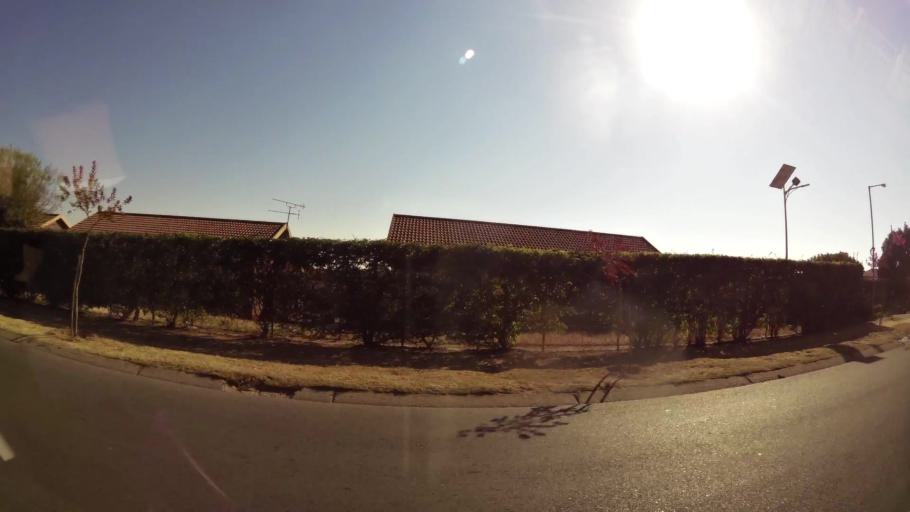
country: ZA
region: Gauteng
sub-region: City of Johannesburg Metropolitan Municipality
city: Modderfontein
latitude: -26.1124
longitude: 28.1242
